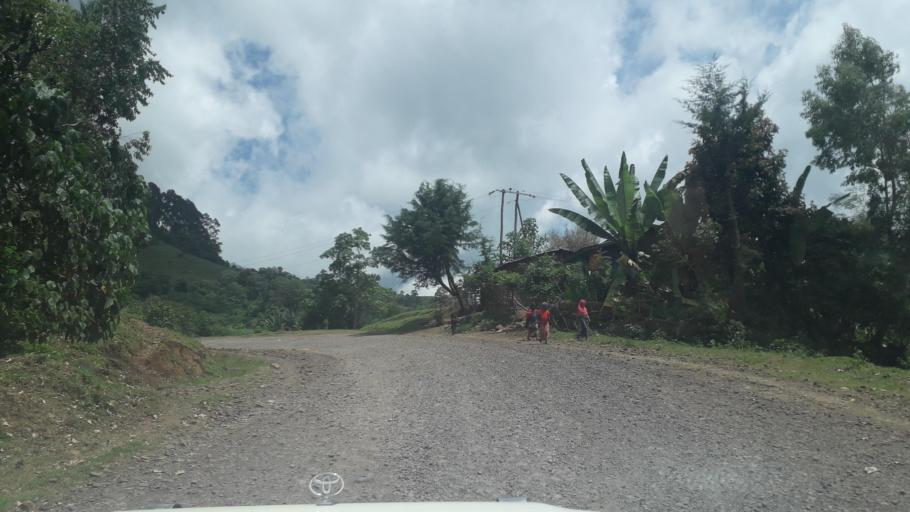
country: ET
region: Oromiya
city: Jima
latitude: 7.4288
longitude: 36.8730
